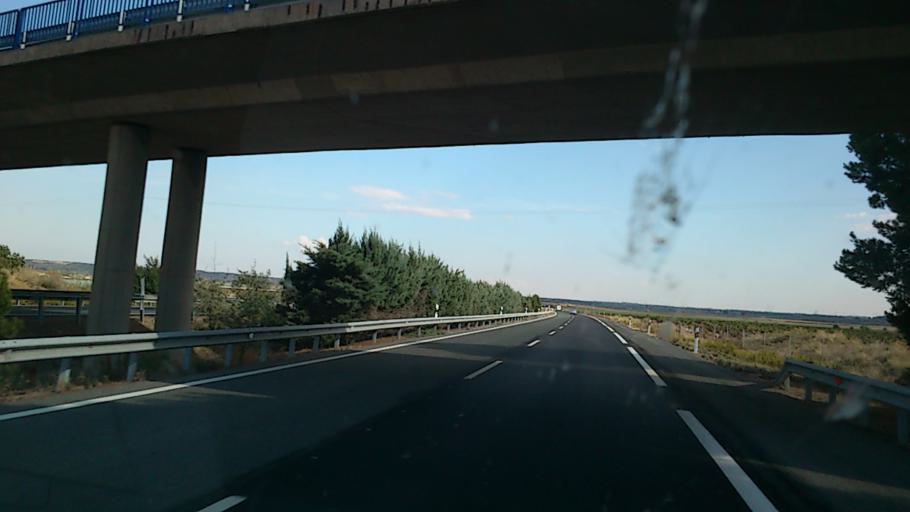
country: ES
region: Navarre
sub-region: Provincia de Navarra
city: Corella
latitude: 42.1540
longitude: -1.8089
